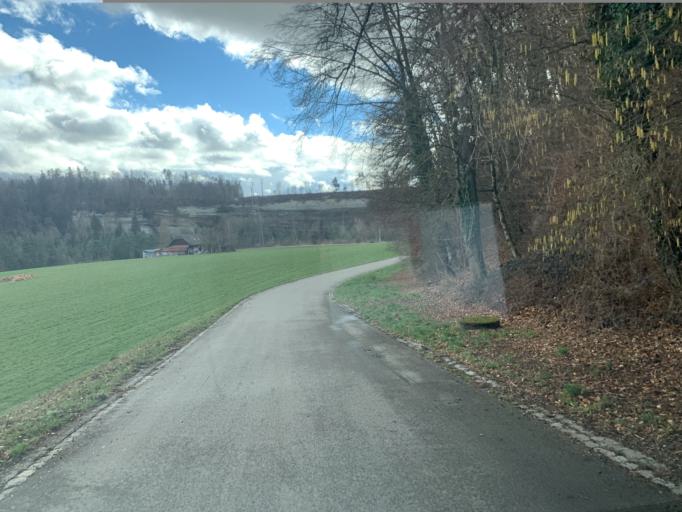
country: CH
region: Fribourg
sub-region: Sense District
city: Bosingen
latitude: 46.8839
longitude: 7.1983
